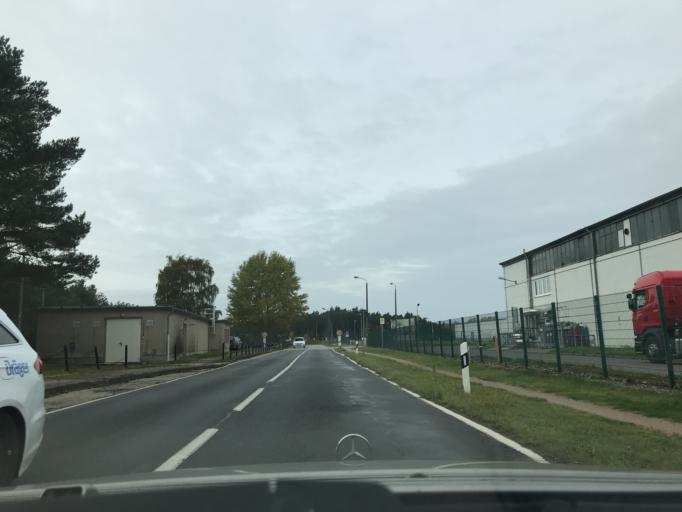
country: DE
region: Mecklenburg-Vorpommern
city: Lubmin
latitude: 54.1383
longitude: 13.6561
